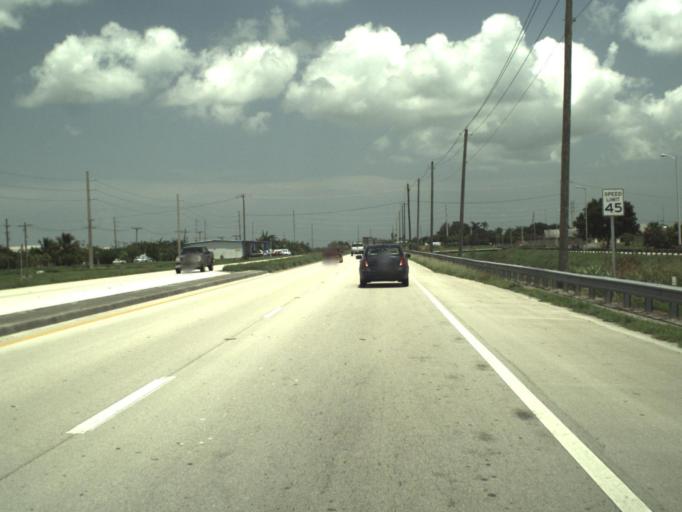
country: US
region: Florida
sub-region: Palm Beach County
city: Belle Glade
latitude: 26.7166
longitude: -80.6680
